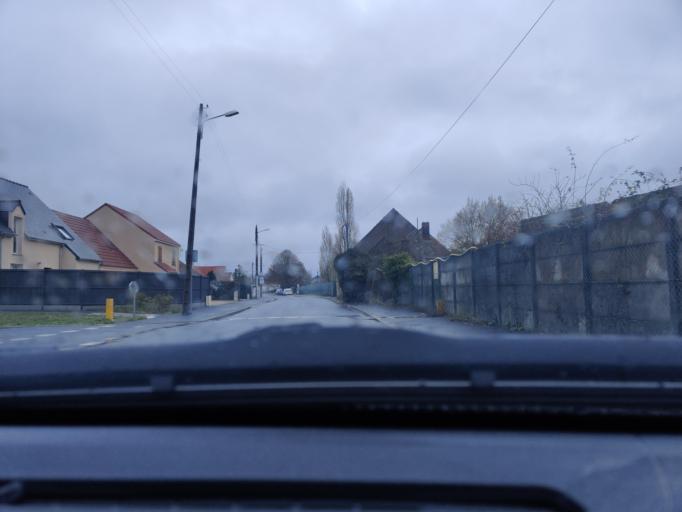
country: FR
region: Centre
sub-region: Departement du Loiret
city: La Chapelle-Saint-Mesmin
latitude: 47.8964
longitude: 1.8266
